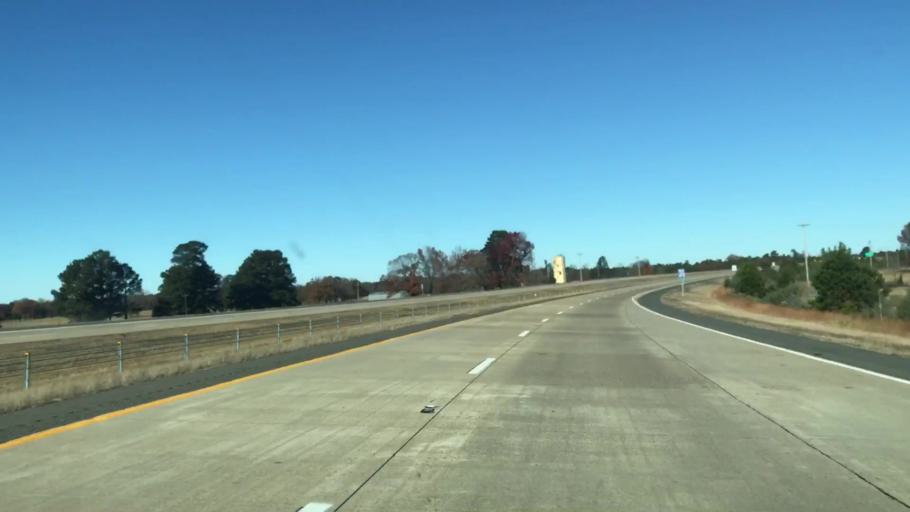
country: US
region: Texas
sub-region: Bowie County
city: Texarkana
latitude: 33.2526
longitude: -93.8915
